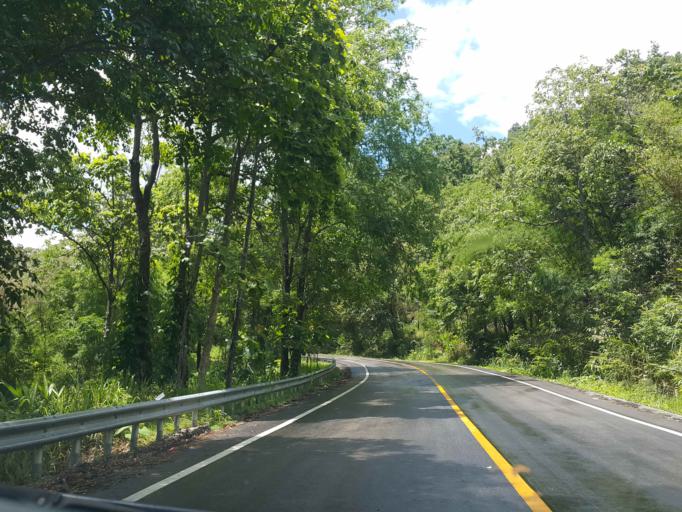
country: TH
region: Chiang Mai
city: Samoeng
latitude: 18.8509
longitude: 98.7719
